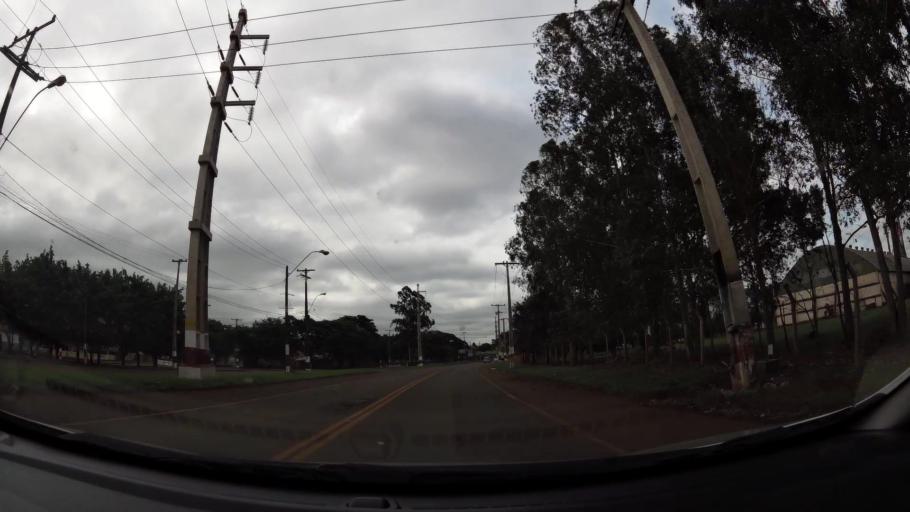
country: PY
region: Alto Parana
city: Ciudad del Este
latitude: -25.3879
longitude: -54.6417
